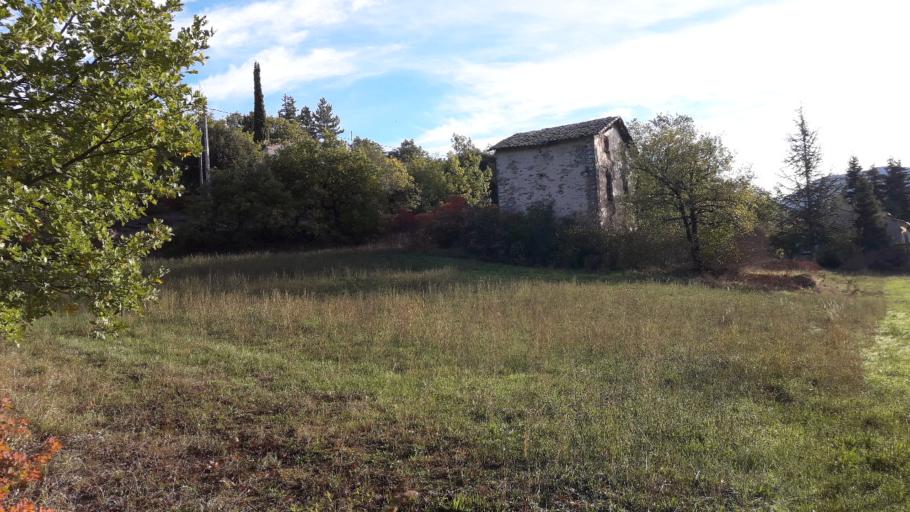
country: FR
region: Provence-Alpes-Cote d'Azur
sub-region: Departement des Alpes-de-Haute-Provence
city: Le Brusquet
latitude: 44.1616
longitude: 6.2983
